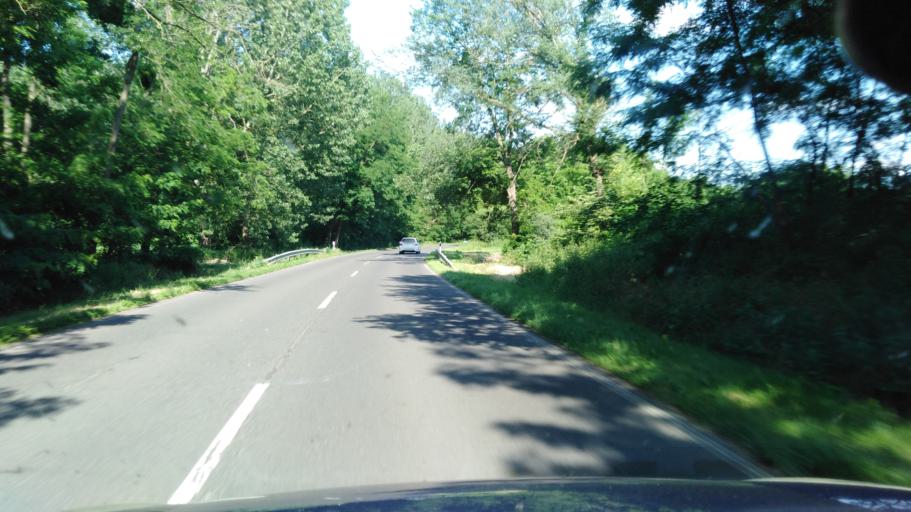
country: HU
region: Szabolcs-Szatmar-Bereg
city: Nyirvasvari
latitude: 47.8117
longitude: 22.2219
